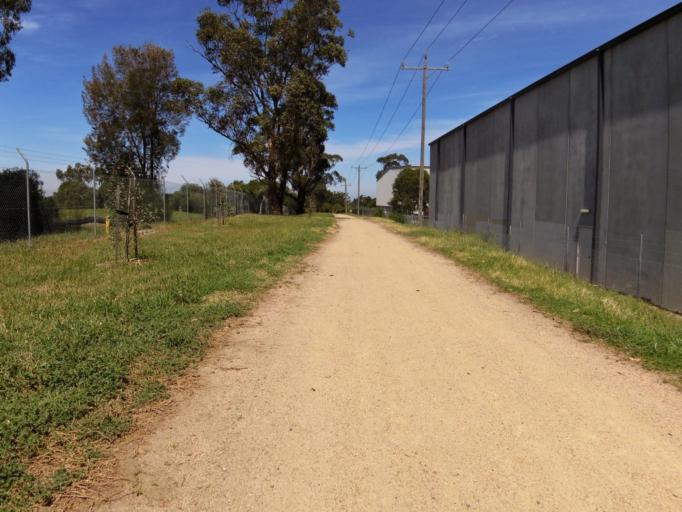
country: AU
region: Victoria
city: Heatherton
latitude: -37.9492
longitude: 145.0867
